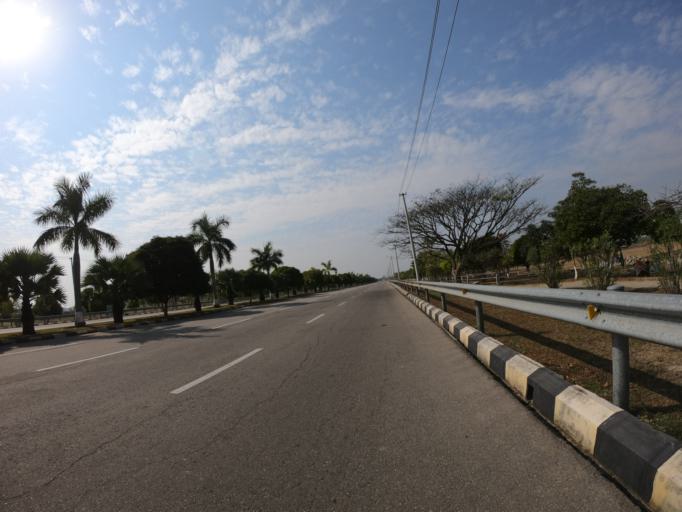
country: MM
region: Mandalay
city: Nay Pyi Taw
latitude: 19.6562
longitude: 96.1325
